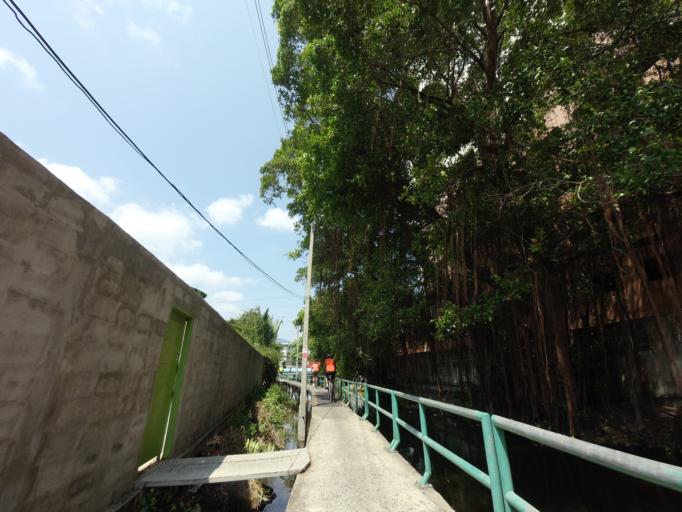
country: TH
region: Bangkok
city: Rat Burana
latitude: 13.6689
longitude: 100.5115
